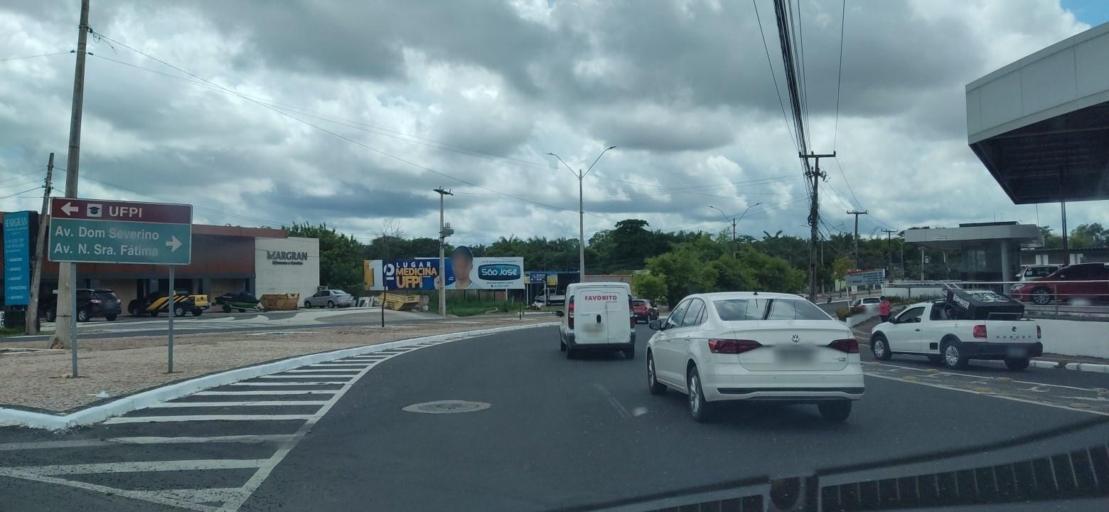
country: BR
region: Piaui
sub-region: Teresina
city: Teresina
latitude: -5.0624
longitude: -42.8041
